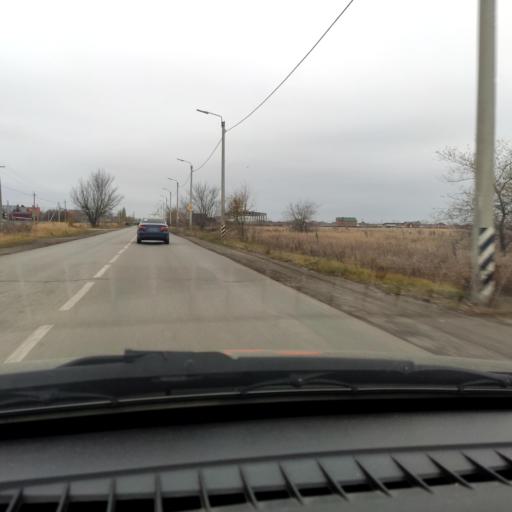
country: RU
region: Samara
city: Podstepki
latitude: 53.5221
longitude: 49.1759
